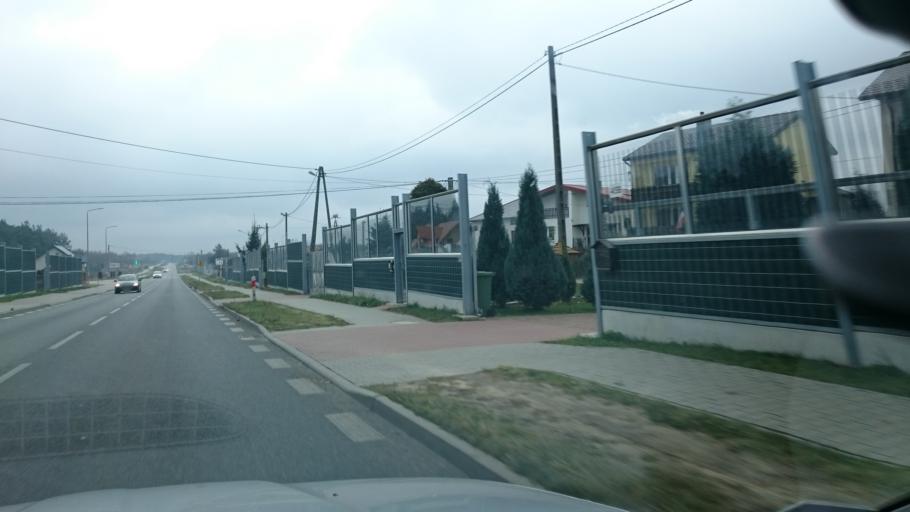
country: PL
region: Swietokrzyskie
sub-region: Powiat konecki
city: Konskie
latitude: 51.1402
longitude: 20.3644
